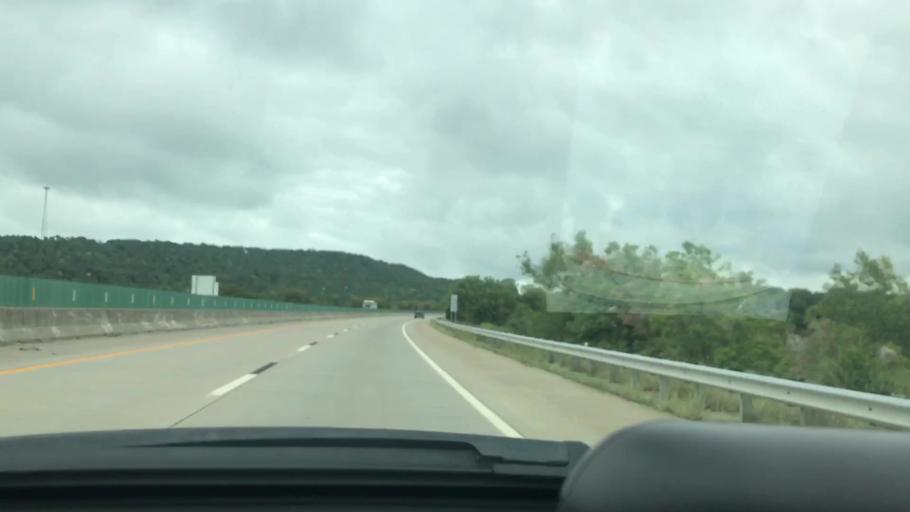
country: US
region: Oklahoma
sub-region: Pittsburg County
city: Krebs
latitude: 35.1088
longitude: -95.6933
